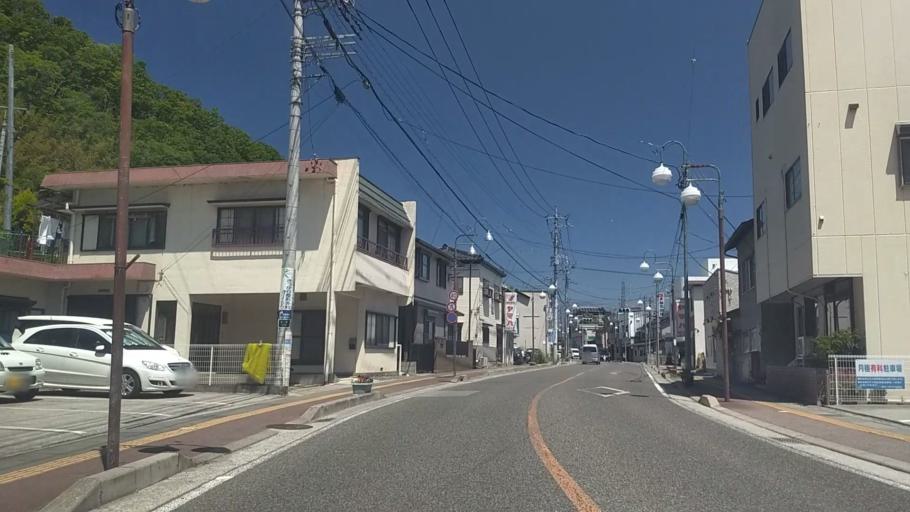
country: JP
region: Yamanashi
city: Nirasaki
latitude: 35.7117
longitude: 138.4495
